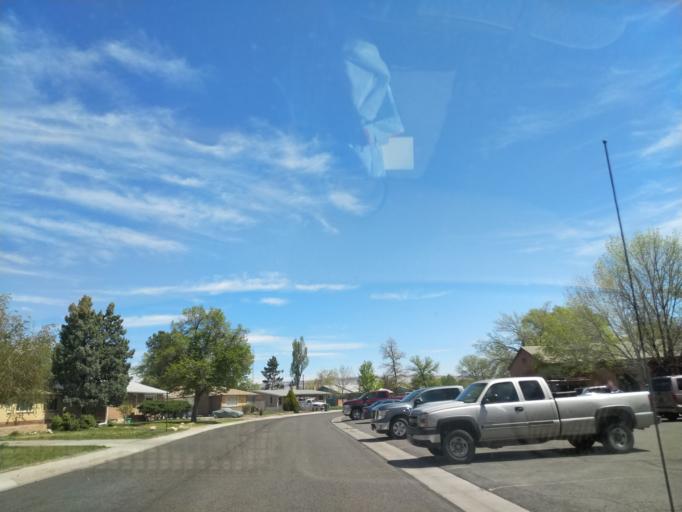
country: US
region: Colorado
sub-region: Mesa County
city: Grand Junction
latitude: 39.0802
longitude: -108.5660
